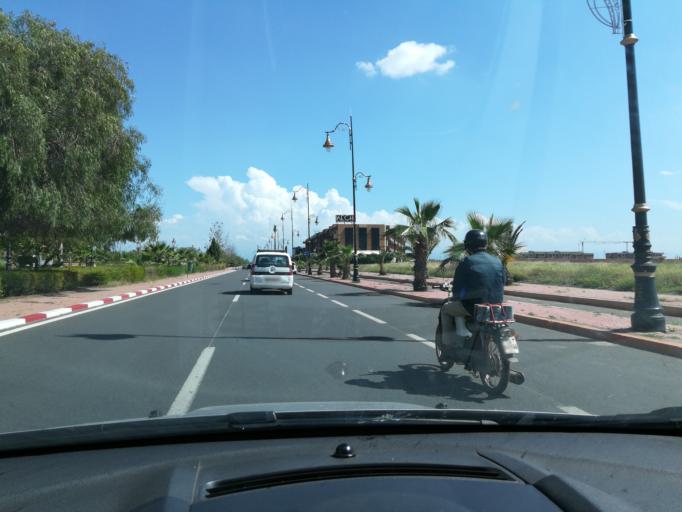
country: MA
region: Marrakech-Tensift-Al Haouz
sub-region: Marrakech
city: Marrakesh
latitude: 31.5890
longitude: -7.9892
